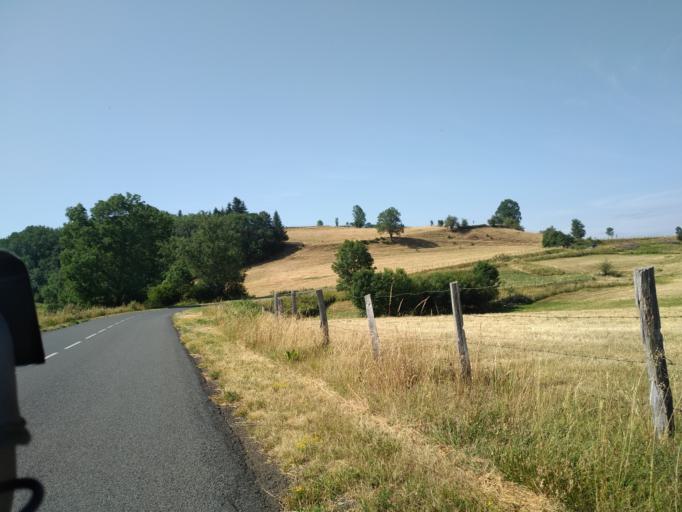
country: FR
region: Auvergne
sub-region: Departement du Cantal
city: Riom-es-Montagnes
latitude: 45.2302
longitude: 2.7313
